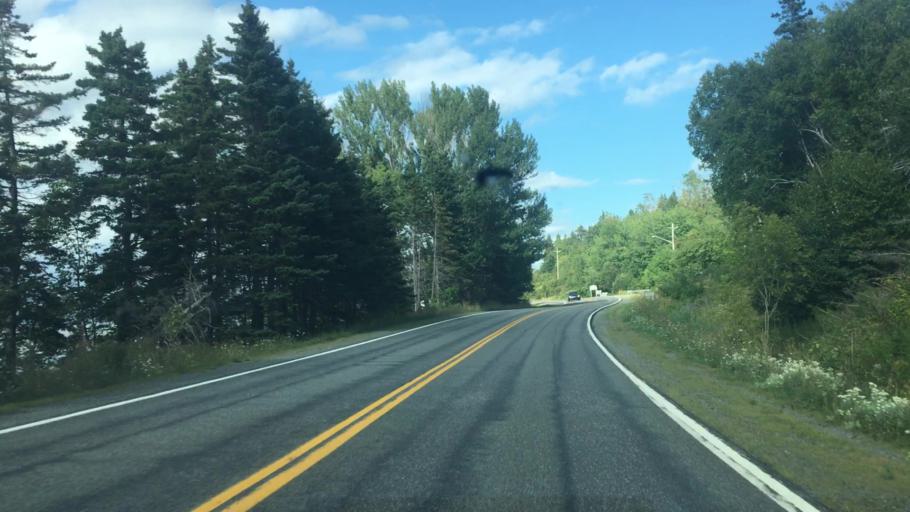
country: CA
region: Nova Scotia
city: Sydney
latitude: 45.8741
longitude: -60.6044
